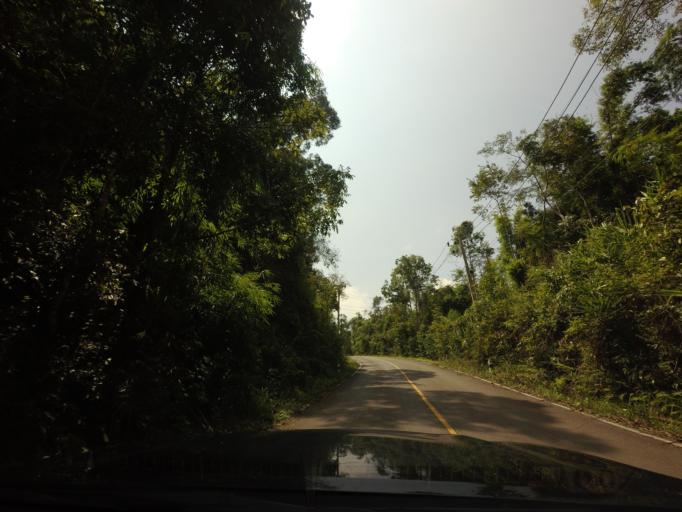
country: TH
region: Loei
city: Na Haeo
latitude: 17.4690
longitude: 100.9313
